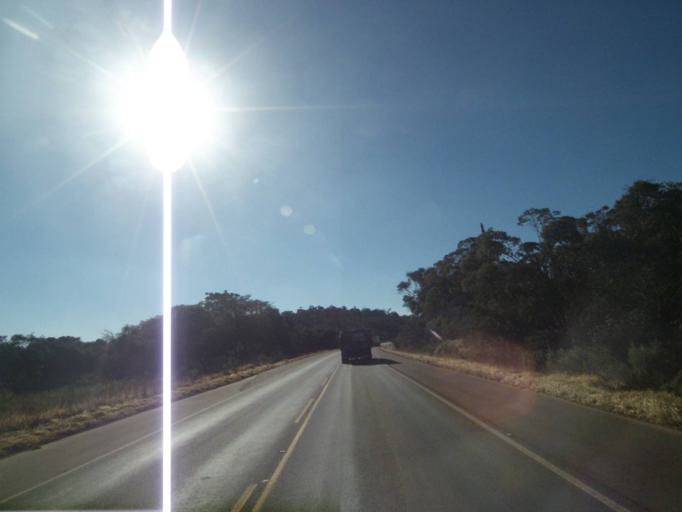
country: BR
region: Parana
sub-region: Tibagi
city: Tibagi
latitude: -24.6557
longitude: -50.4531
